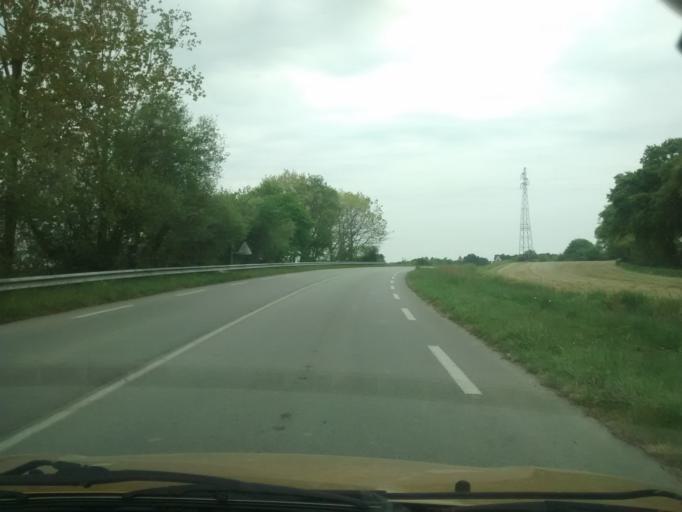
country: FR
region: Brittany
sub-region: Departement du Morbihan
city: Ambon
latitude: 47.5938
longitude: -2.5490
